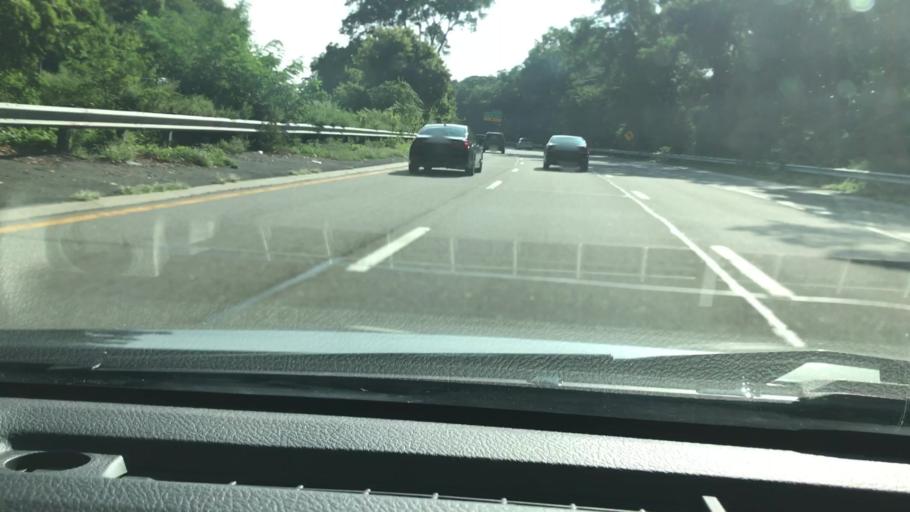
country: US
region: New York
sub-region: Nassau County
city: Lakeview
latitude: 40.6826
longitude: -73.6502
